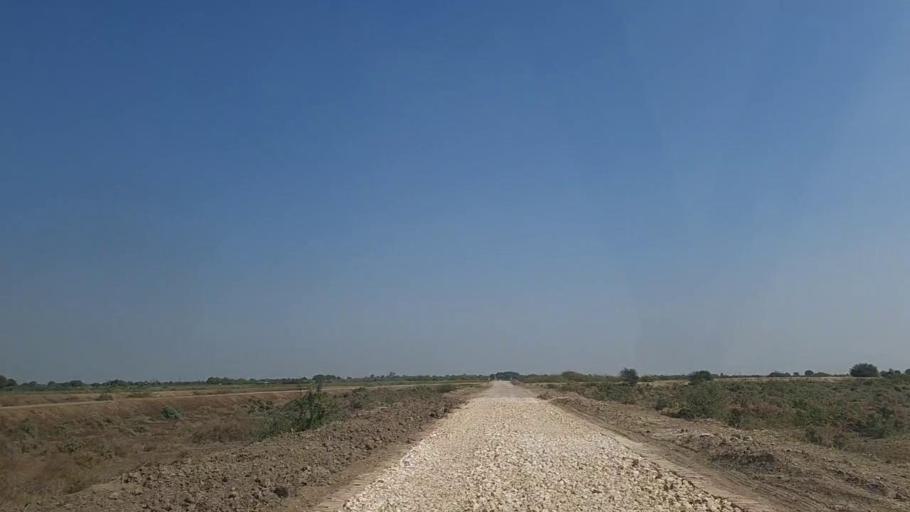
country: PK
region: Sindh
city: Digri
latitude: 25.1615
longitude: 69.1810
